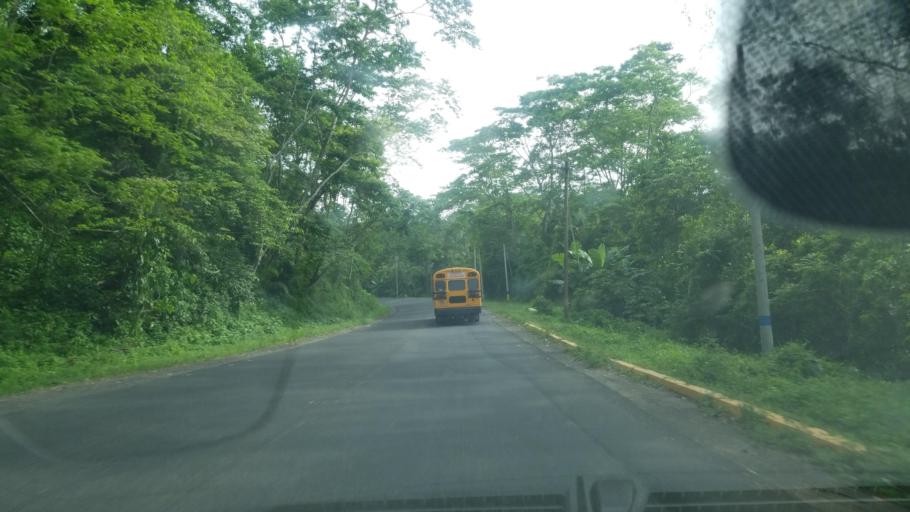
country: HN
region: Santa Barbara
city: Petoa
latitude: 15.2184
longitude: -88.2684
